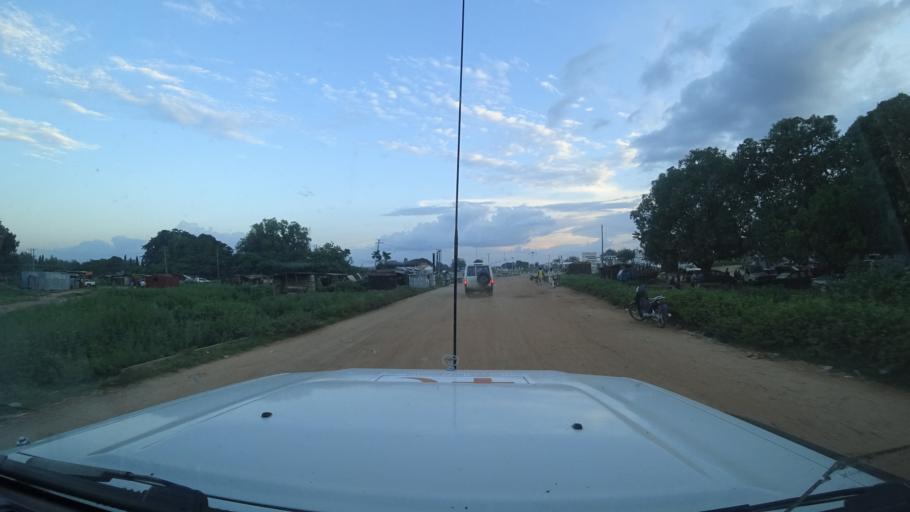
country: NG
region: Niger
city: Minna
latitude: 9.6373
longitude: 6.5797
